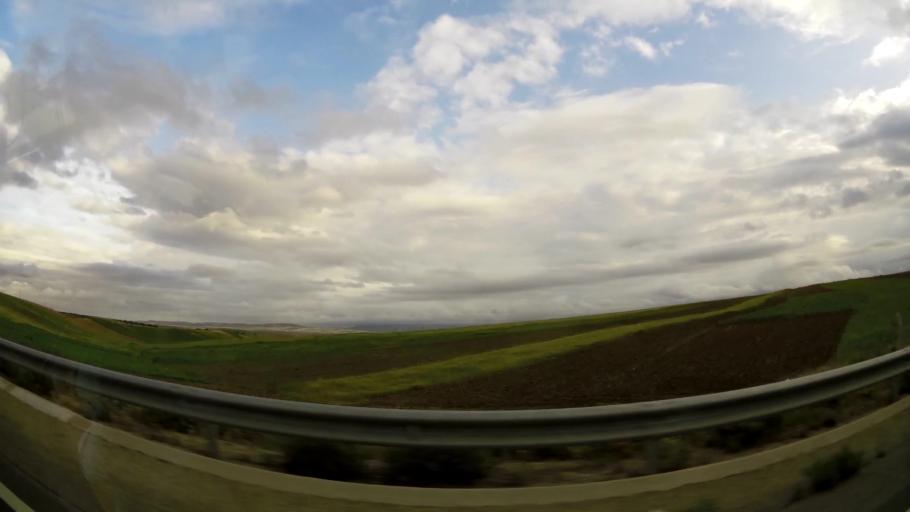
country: MA
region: Taza-Al Hoceima-Taounate
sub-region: Taza
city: Taza
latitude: 34.2513
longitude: -3.9018
